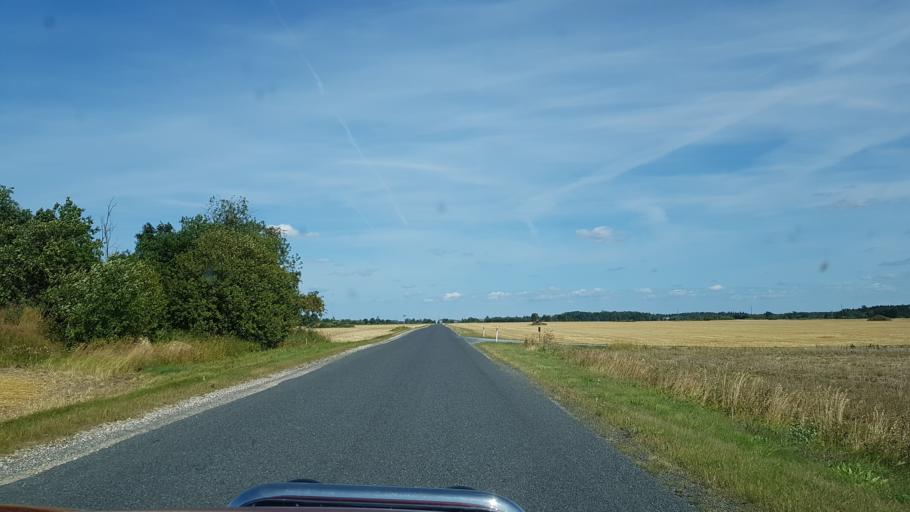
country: EE
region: Laeaene-Virumaa
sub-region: Rakke vald
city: Rakke
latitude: 59.0419
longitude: 26.3550
